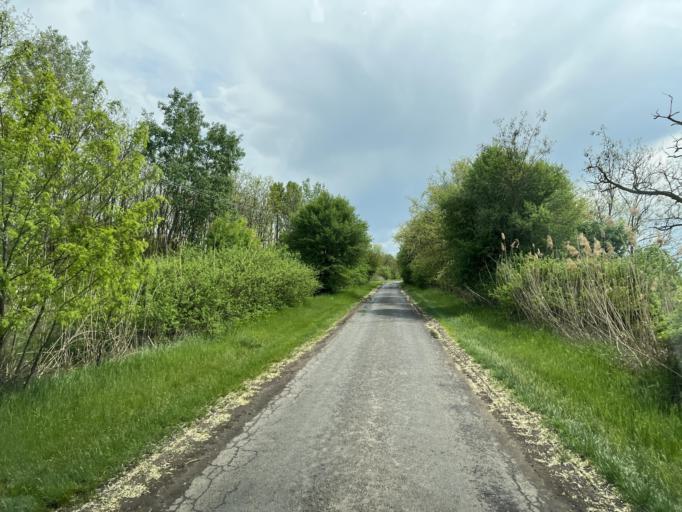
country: HU
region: Pest
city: Nagykoros
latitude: 46.9702
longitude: 19.8182
